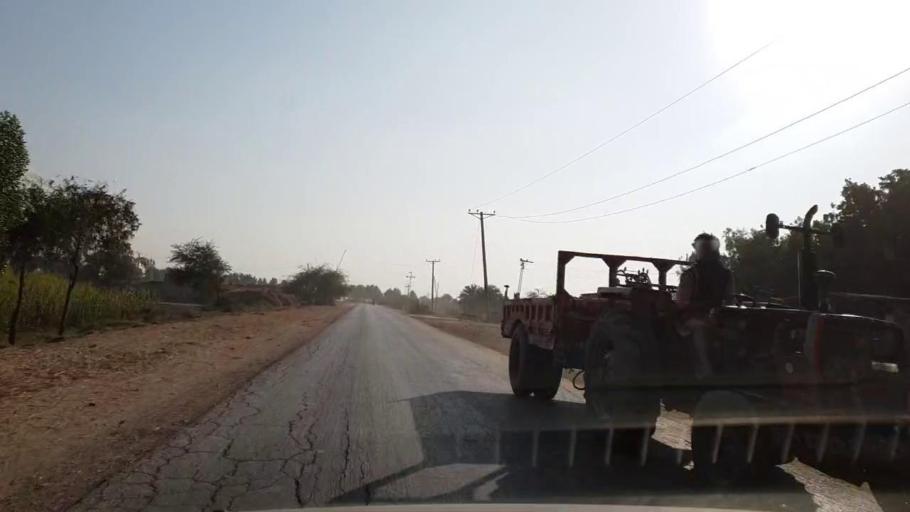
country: PK
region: Sindh
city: Bulri
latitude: 24.8676
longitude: 68.3381
